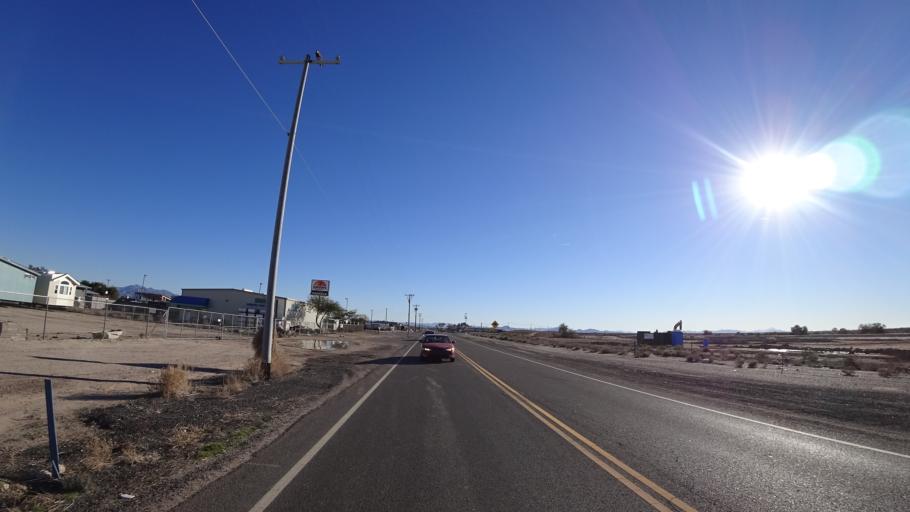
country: US
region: Arizona
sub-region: Maricopa County
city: Citrus Park
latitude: 33.4591
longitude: -112.4788
